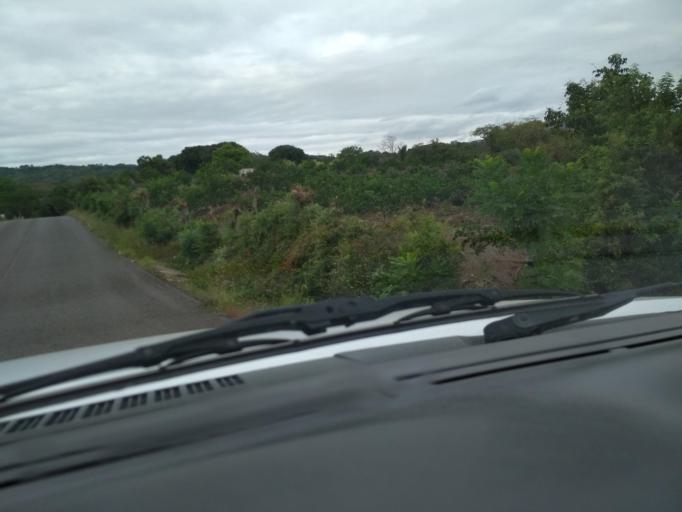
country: MX
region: Veracruz
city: Alto Lucero
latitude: 19.5949
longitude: -96.7828
